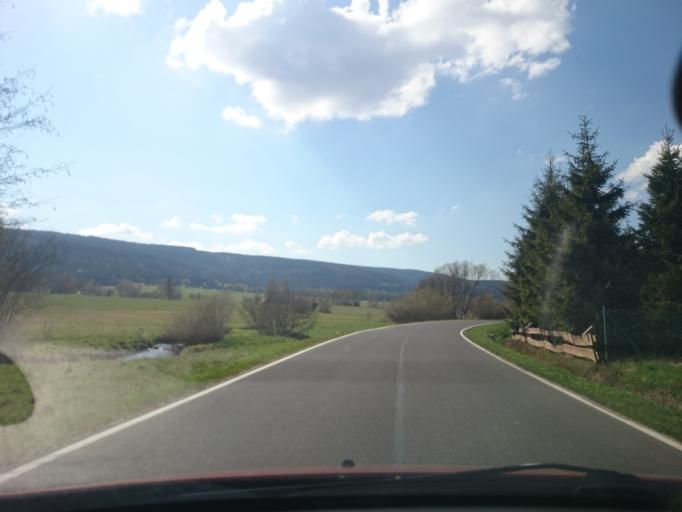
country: PL
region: Lower Silesian Voivodeship
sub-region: Powiat klodzki
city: Szczytna
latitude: 50.2975
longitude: 16.4621
